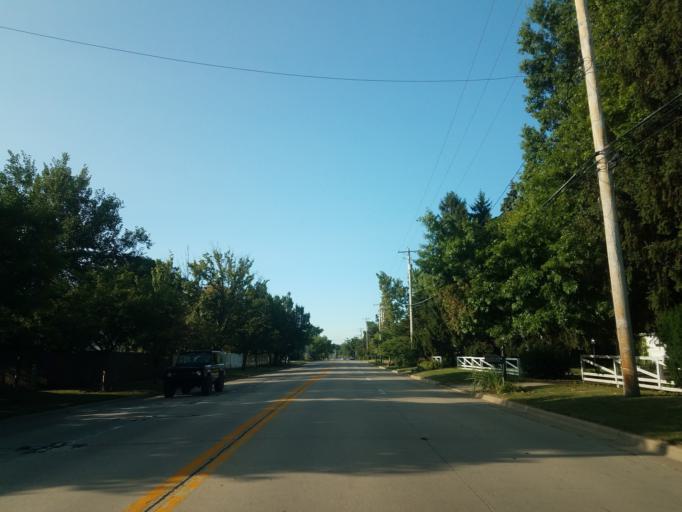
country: US
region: Illinois
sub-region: McLean County
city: Normal
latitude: 40.5305
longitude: -88.9832
